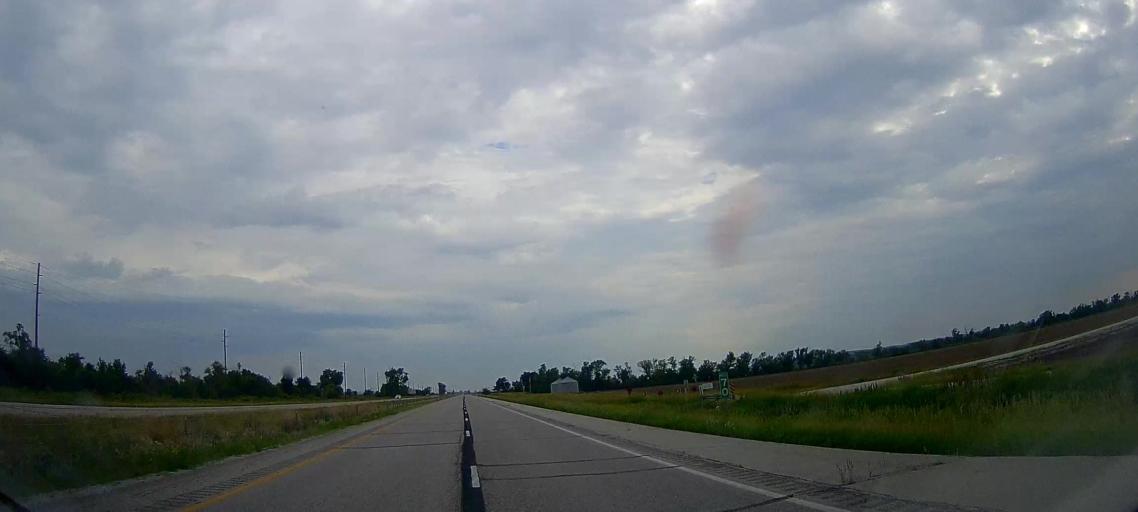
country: US
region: Iowa
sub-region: Harrison County
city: Missouri Valley
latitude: 41.4711
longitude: -95.8998
